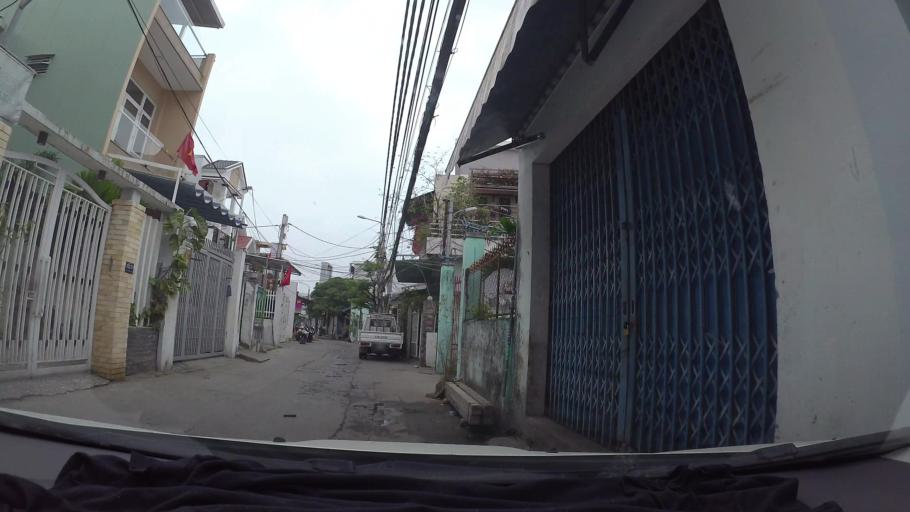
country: VN
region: Da Nang
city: Thanh Khe
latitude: 16.0623
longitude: 108.1875
